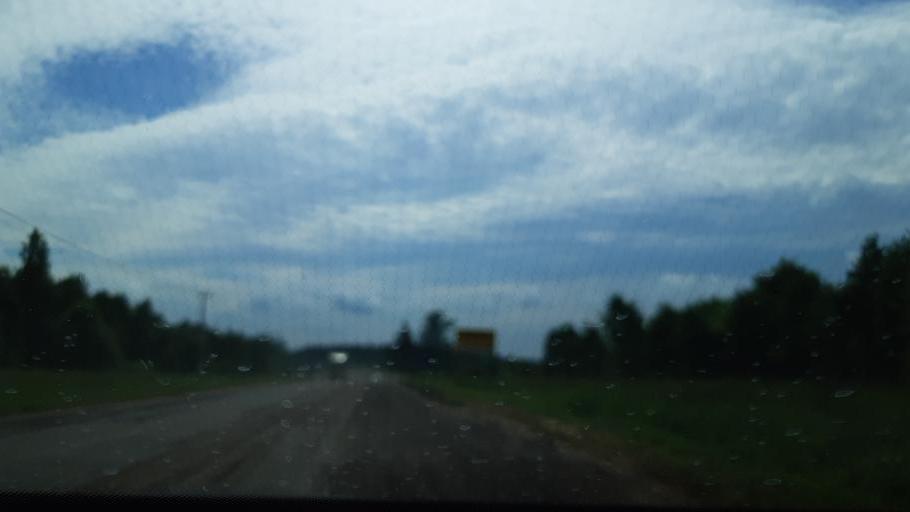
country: RU
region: Moskovskaya
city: Vereya
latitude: 55.2439
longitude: 36.0464
